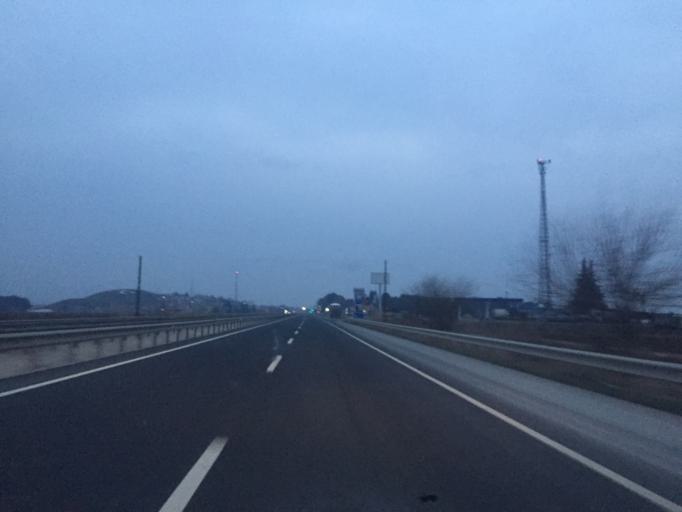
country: TR
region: Sanliurfa
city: Camlidere
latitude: 37.1554
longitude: 39.0557
